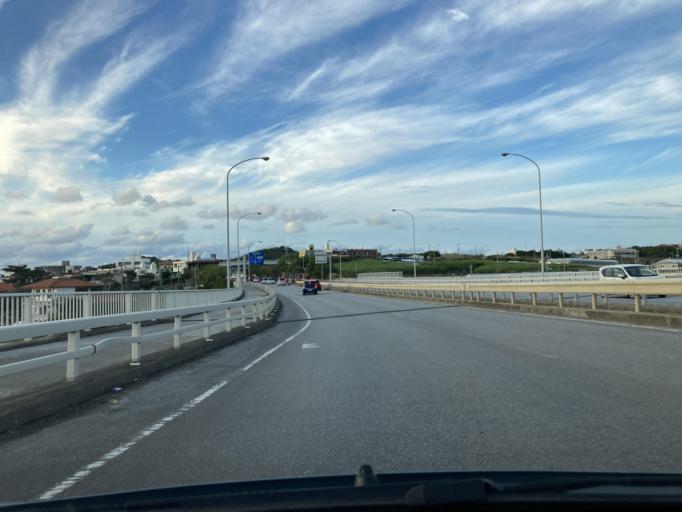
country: JP
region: Okinawa
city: Tomigusuku
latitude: 26.1767
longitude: 127.7270
